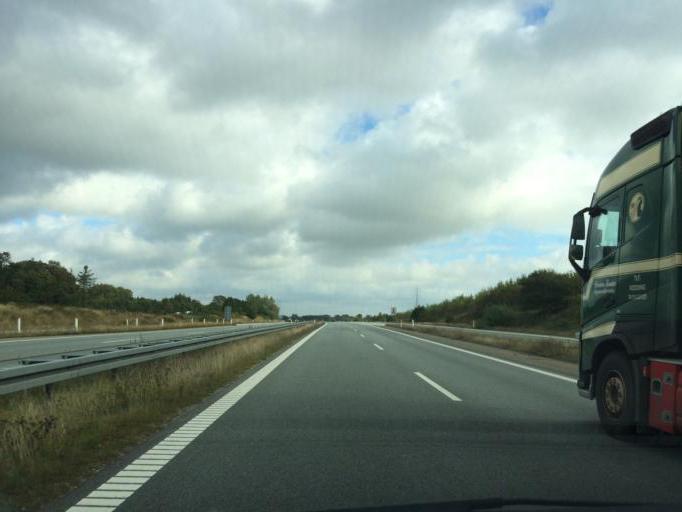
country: DK
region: North Denmark
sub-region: Alborg Kommune
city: Vodskov
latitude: 57.1150
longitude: 10.0595
